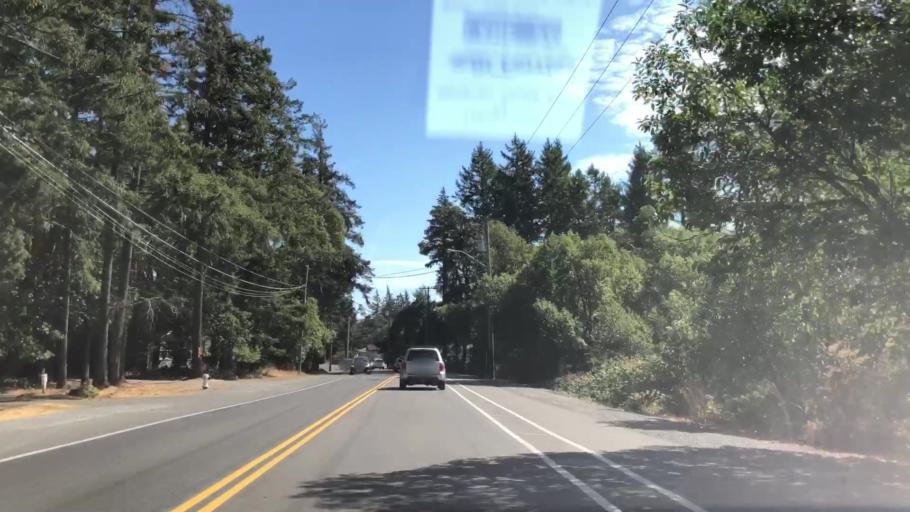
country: CA
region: British Columbia
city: Colwood
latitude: 48.4295
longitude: -123.4941
